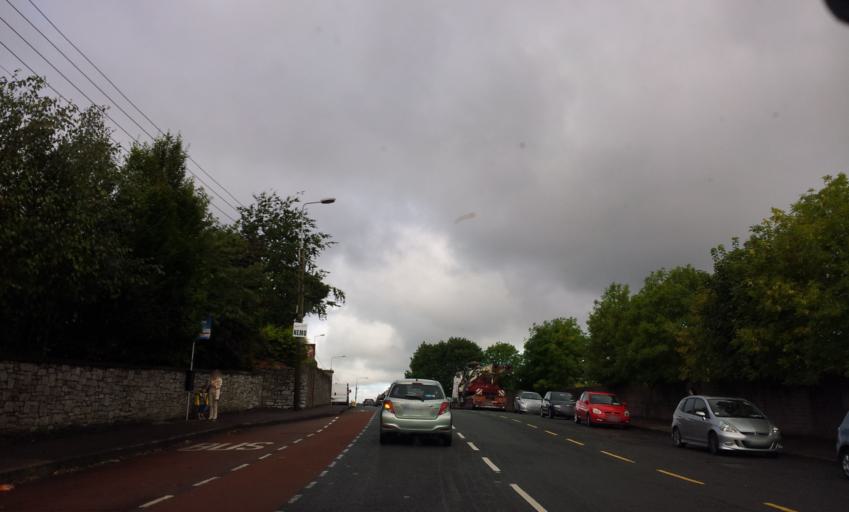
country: IE
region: Munster
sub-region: County Cork
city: Cork
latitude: 51.8801
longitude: -8.4478
